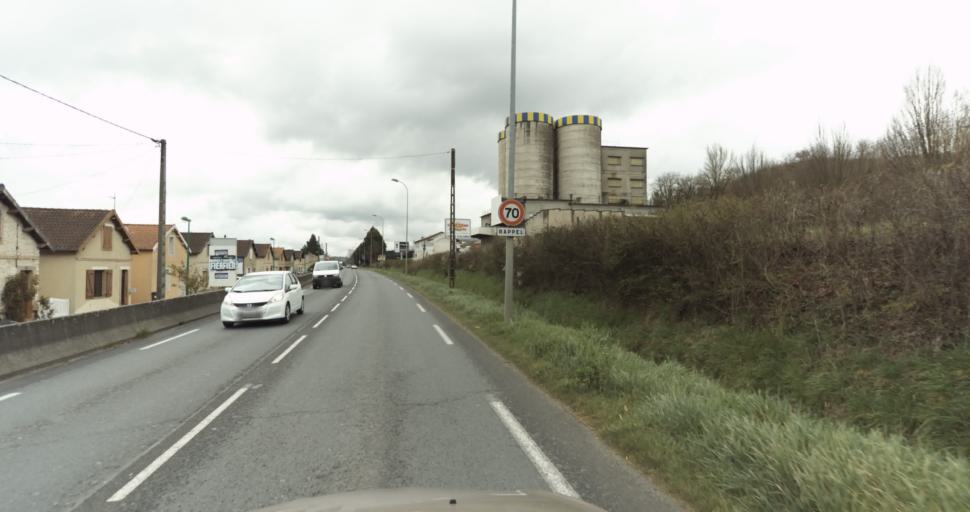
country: FR
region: Midi-Pyrenees
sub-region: Departement du Tarn
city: Puygouzon
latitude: 43.9038
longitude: 2.1430
